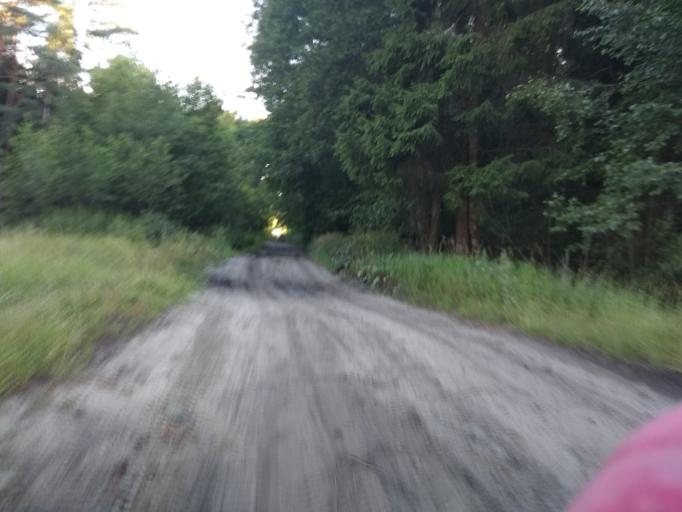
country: RU
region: Moskovskaya
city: Misheronskiy
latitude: 55.7243
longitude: 39.7493
